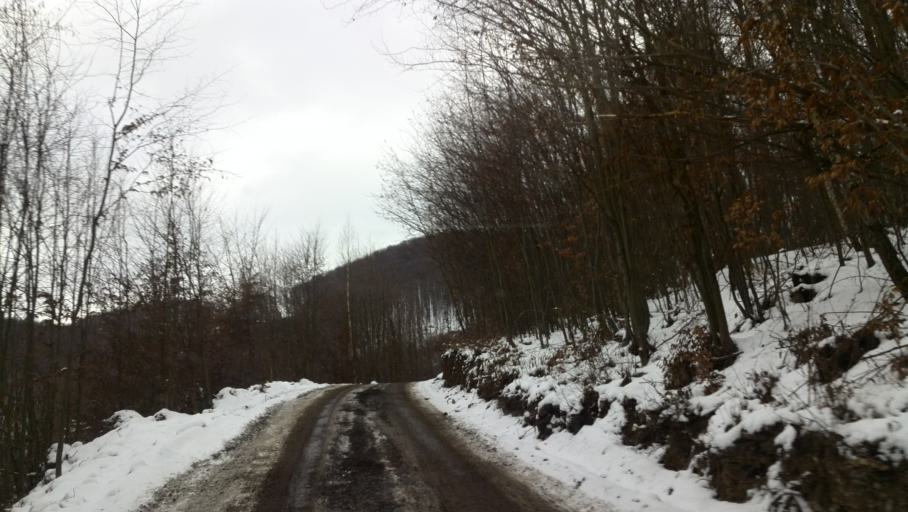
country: SK
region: Kosicky
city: Gelnica
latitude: 48.8184
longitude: 21.0699
